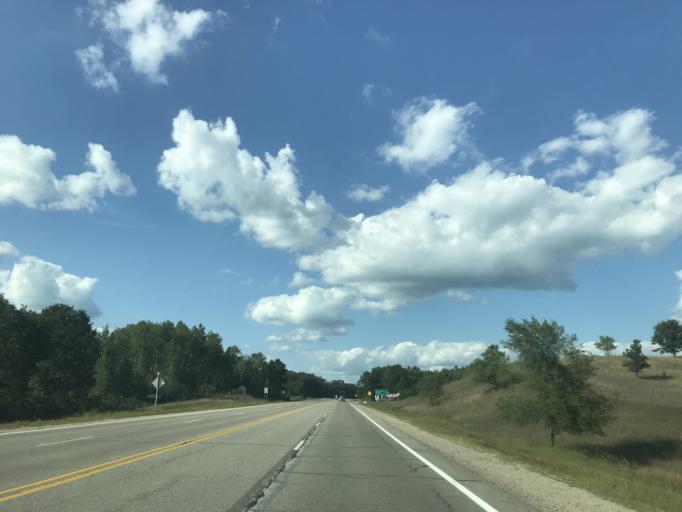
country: US
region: Michigan
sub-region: Newaygo County
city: Newaygo
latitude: 43.4283
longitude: -85.7961
